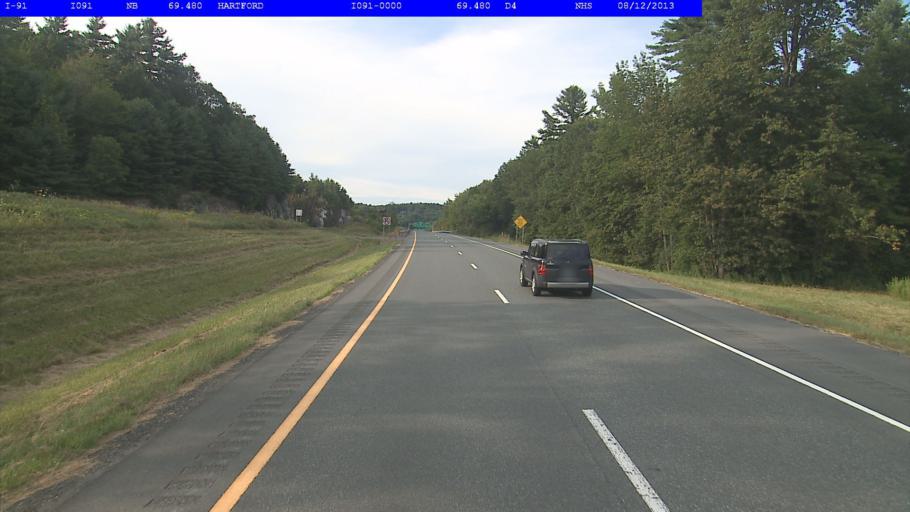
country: US
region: Vermont
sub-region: Windsor County
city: White River Junction
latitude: 43.6350
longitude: -72.3386
